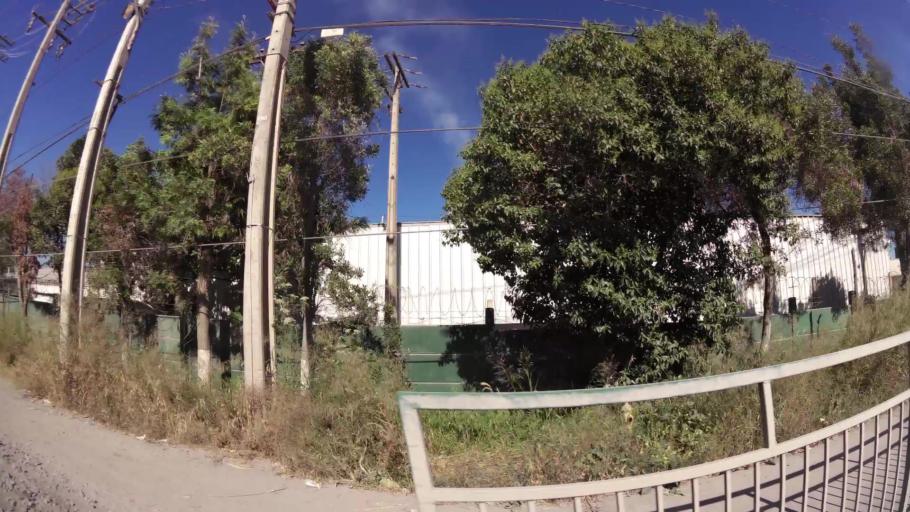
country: CL
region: Santiago Metropolitan
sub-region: Provincia de Maipo
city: San Bernardo
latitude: -33.5564
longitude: -70.6957
